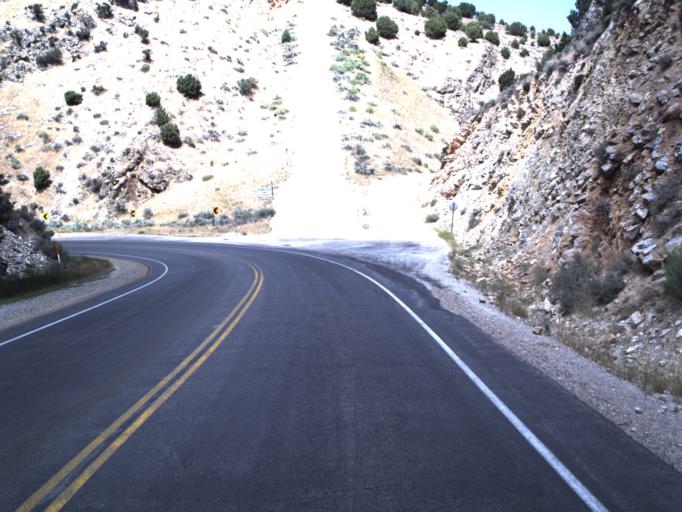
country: US
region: Utah
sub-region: Rich County
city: Randolph
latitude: 41.8241
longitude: -111.2925
